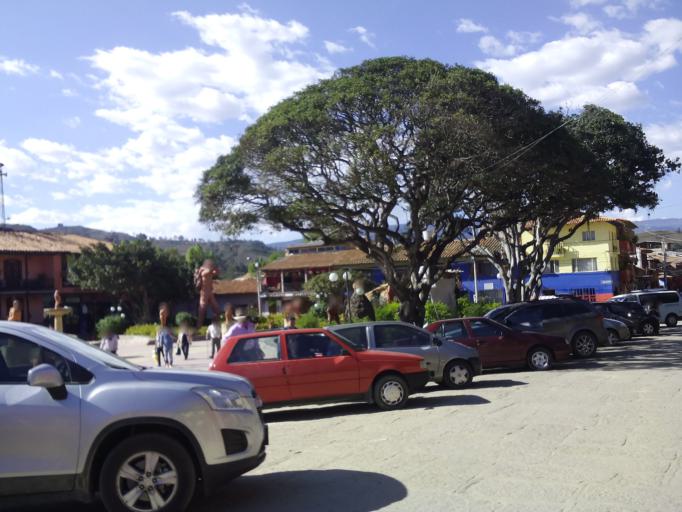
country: CO
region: Boyaca
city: Raquira
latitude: 5.5379
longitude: -73.6328
